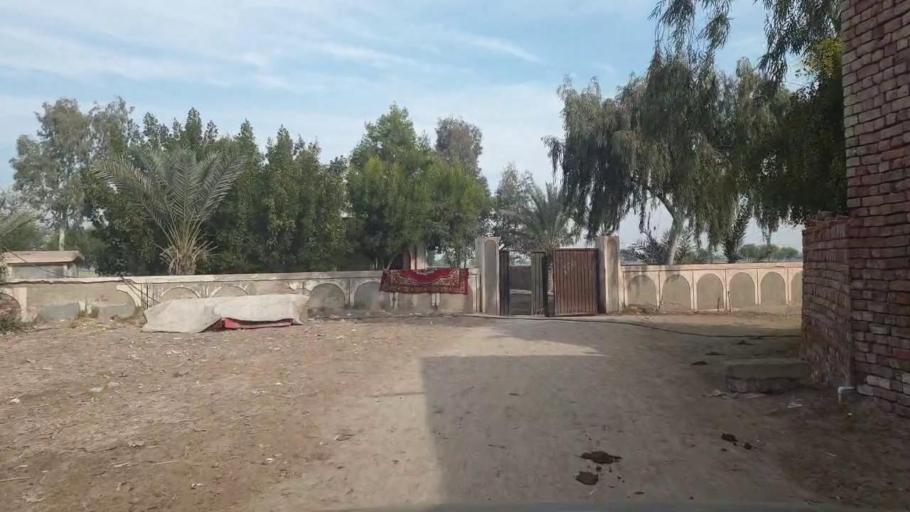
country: PK
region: Sindh
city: Khadro
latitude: 26.1595
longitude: 68.6961
